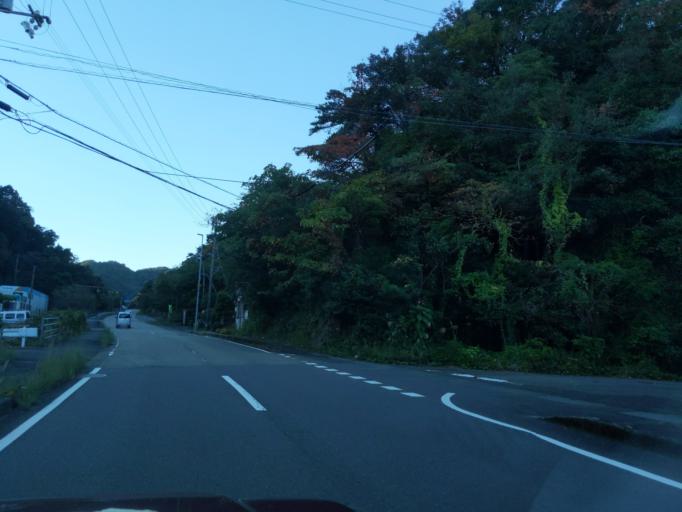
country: JP
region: Kochi
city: Muroto-misakicho
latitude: 33.5927
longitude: 134.3526
